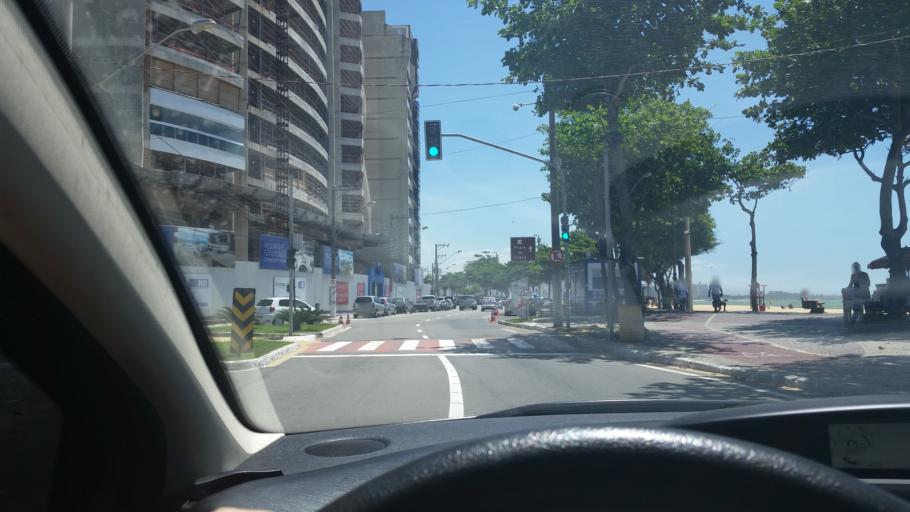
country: BR
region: Espirito Santo
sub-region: Vila Velha
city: Vila Velha
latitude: -20.3527
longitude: -40.2840
